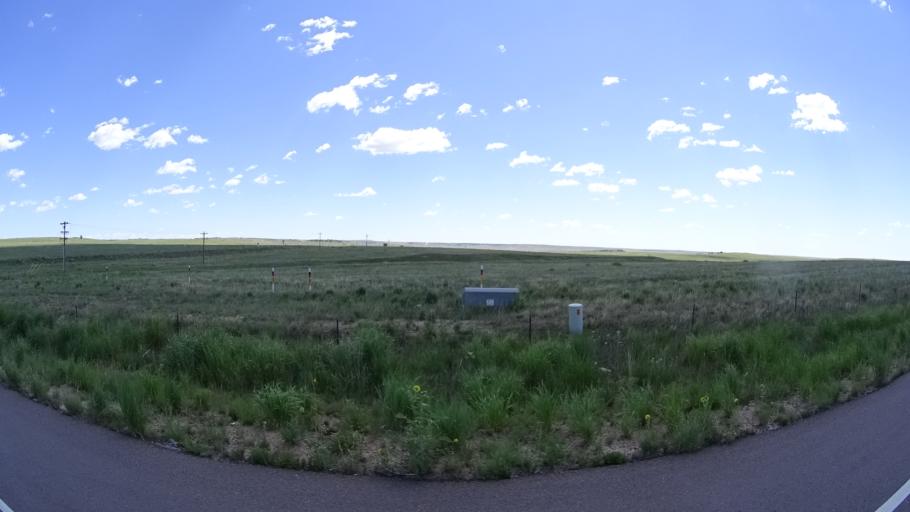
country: US
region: Colorado
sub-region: El Paso County
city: Cimarron Hills
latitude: 38.8367
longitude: -104.6827
